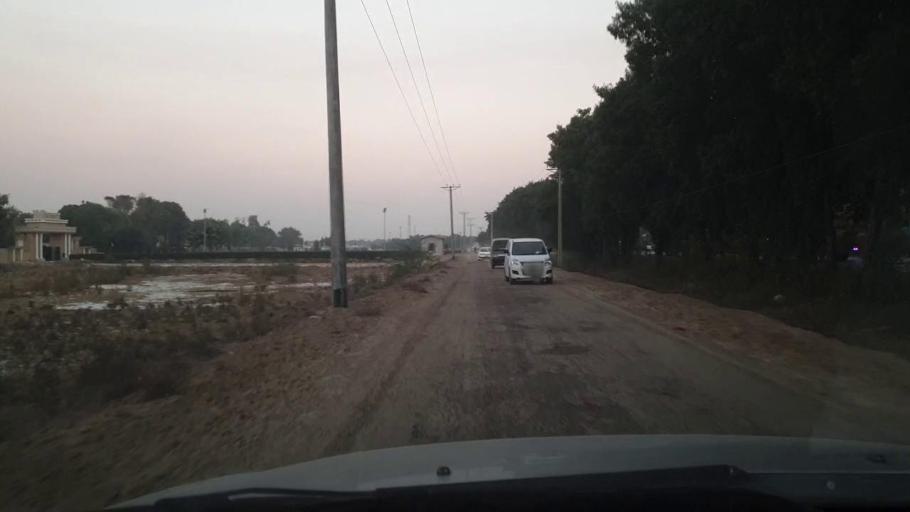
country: PK
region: Sindh
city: Mirpur Mathelo
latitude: 28.0278
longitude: 69.5779
